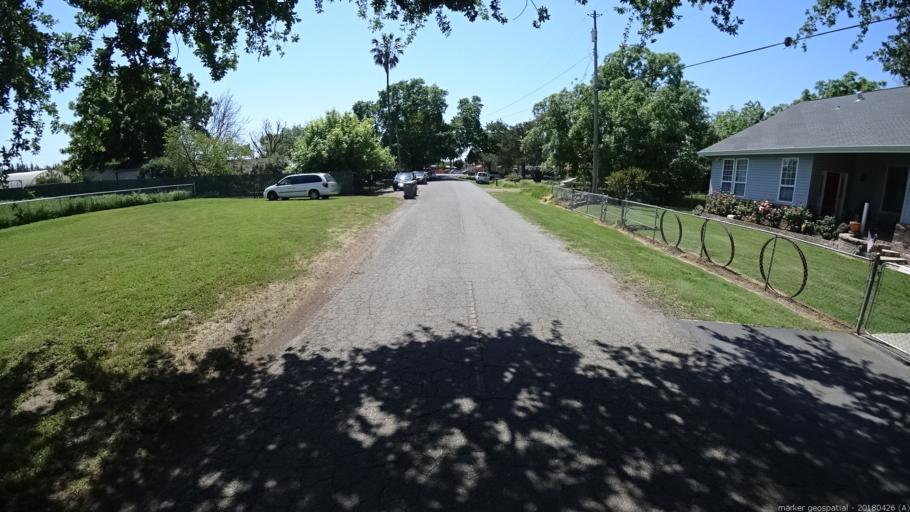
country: US
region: California
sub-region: Yolo County
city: West Sacramento
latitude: 38.5335
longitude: -121.5493
